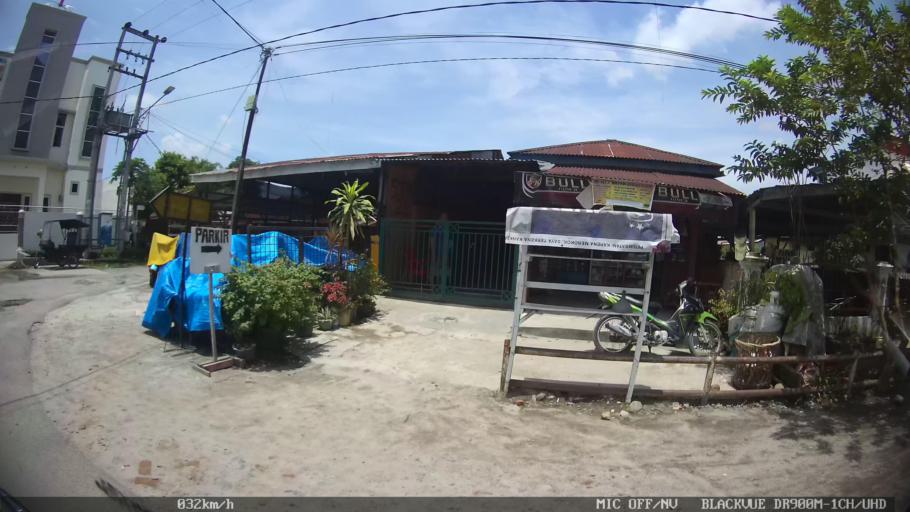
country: ID
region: North Sumatra
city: Perbaungan
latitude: 3.5415
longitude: 98.8790
